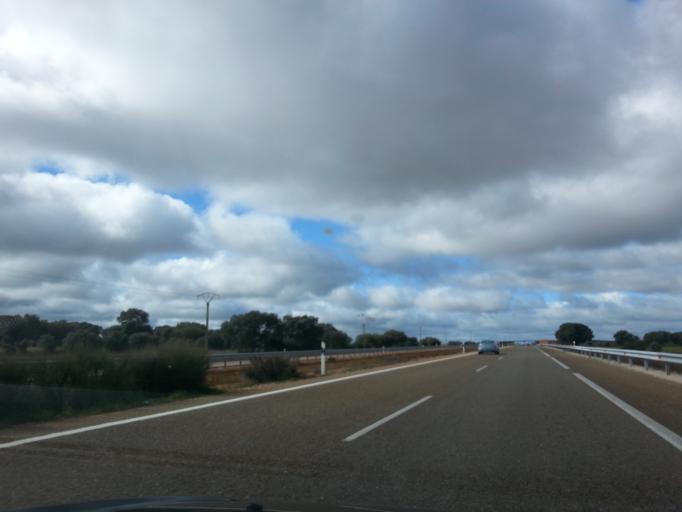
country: ES
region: Castille and Leon
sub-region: Provincia de Salamanca
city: Galindo y Perahuy
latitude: 40.9257
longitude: -5.8330
